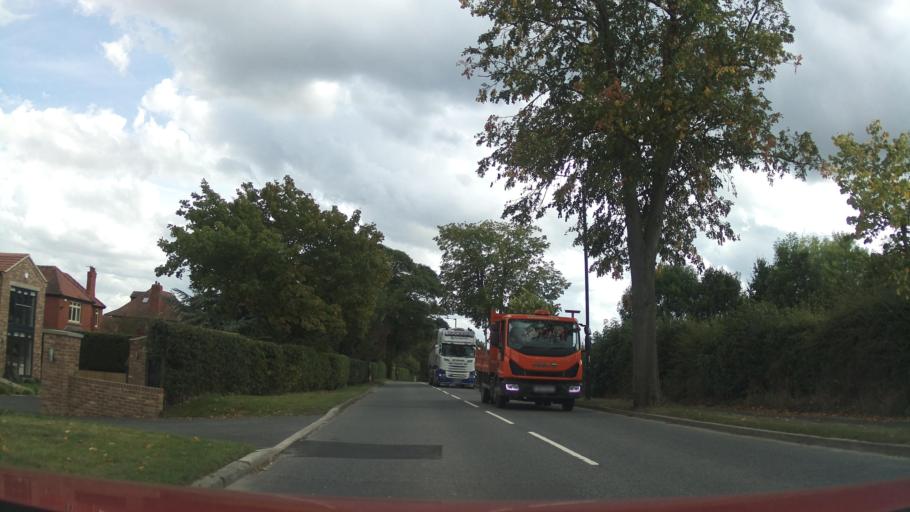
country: GB
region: England
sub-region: North Yorkshire
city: Ripon
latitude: 54.1497
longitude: -1.5313
